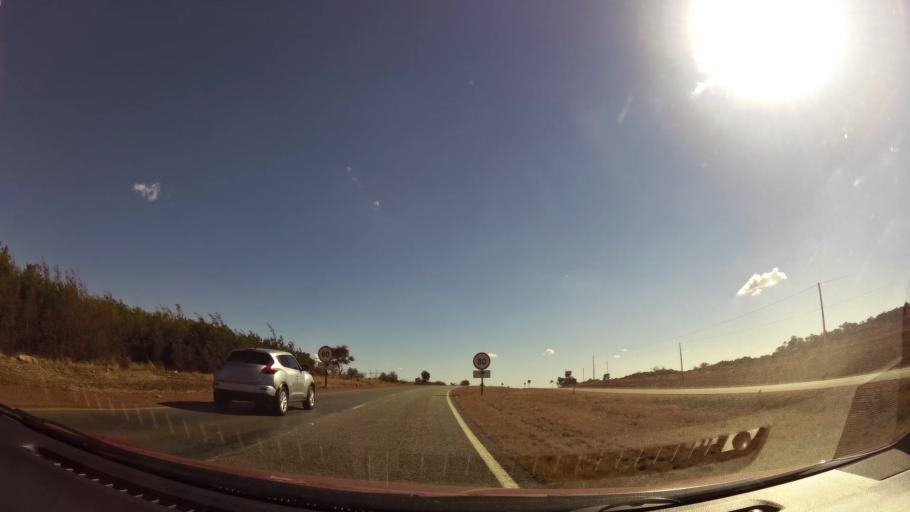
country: ZA
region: Gauteng
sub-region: West Rand District Municipality
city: Carletonville
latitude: -26.4173
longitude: 27.4404
